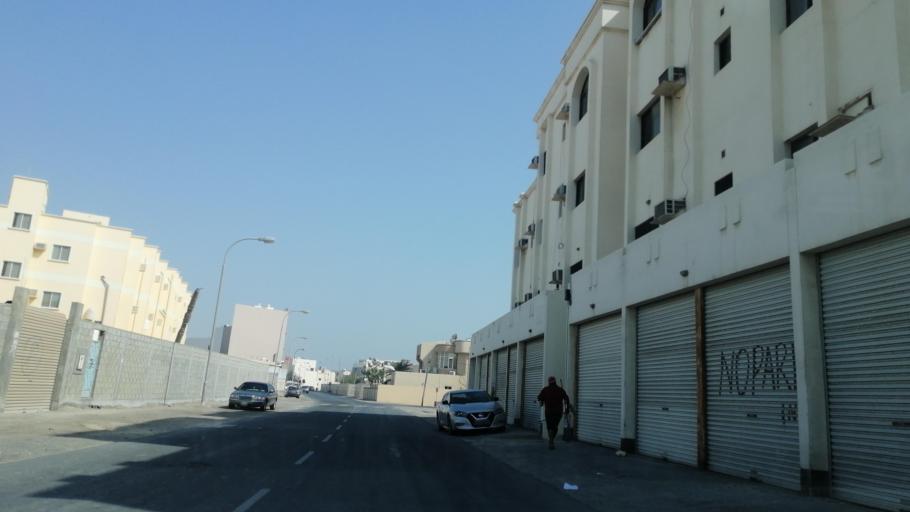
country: BH
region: Muharraq
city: Al Hadd
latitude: 26.2546
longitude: 50.6359
